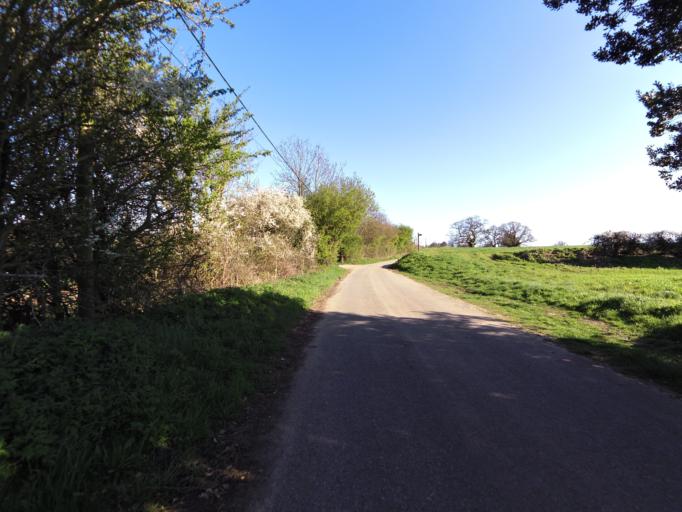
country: GB
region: England
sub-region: Suffolk
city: Bramford
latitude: 52.0557
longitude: 1.1054
